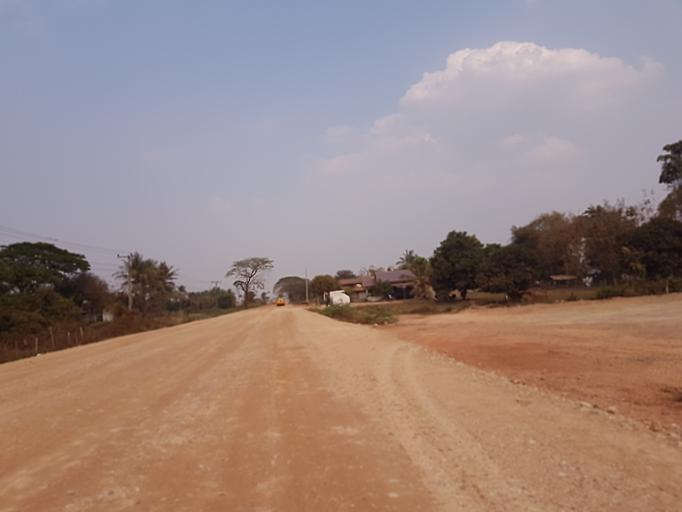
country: TH
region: Nong Khai
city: Nong Khai
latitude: 17.9794
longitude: 102.8740
